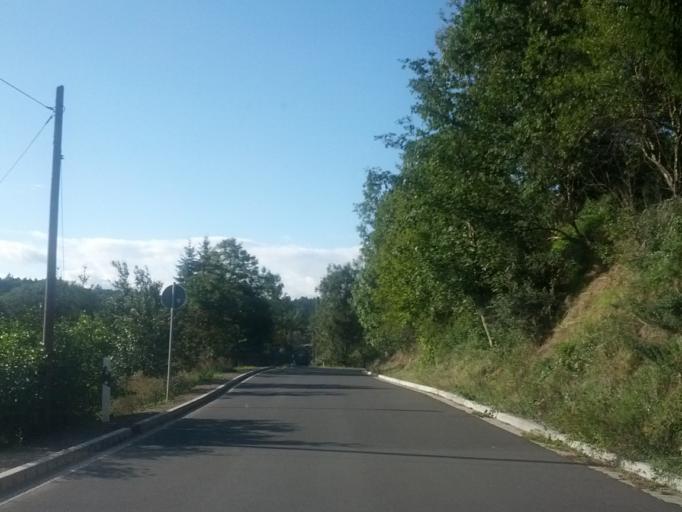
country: DE
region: Thuringia
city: Lauchroden
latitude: 50.9686
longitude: 10.1596
